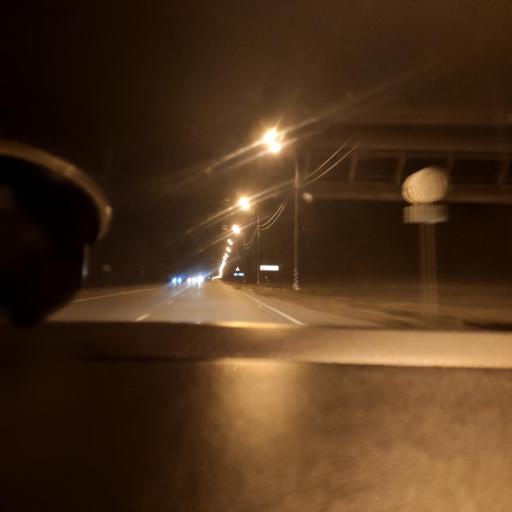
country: RU
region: Moskovskaya
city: Bronnitsy
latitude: 55.3830
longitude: 38.3612
